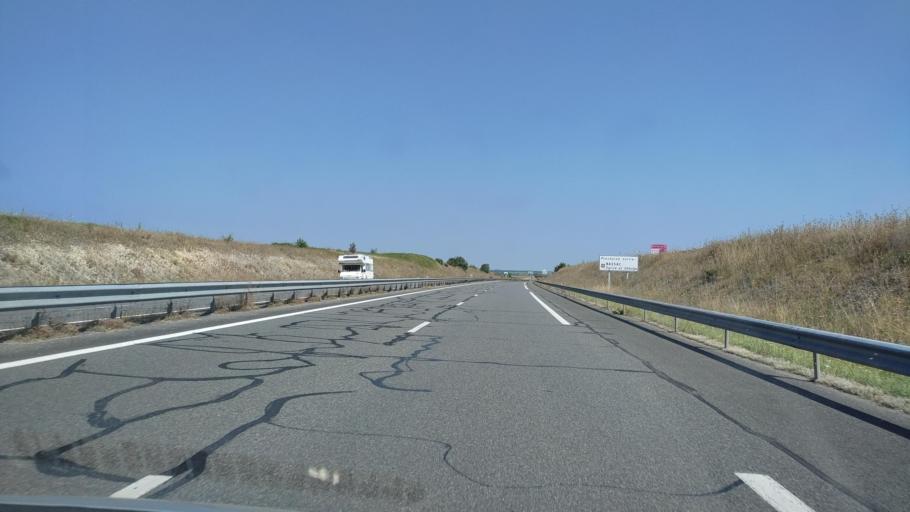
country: FR
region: Poitou-Charentes
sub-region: Departement de la Charente
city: Saint-Meme-les-Carrieres
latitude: 45.6935
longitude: -0.0969
